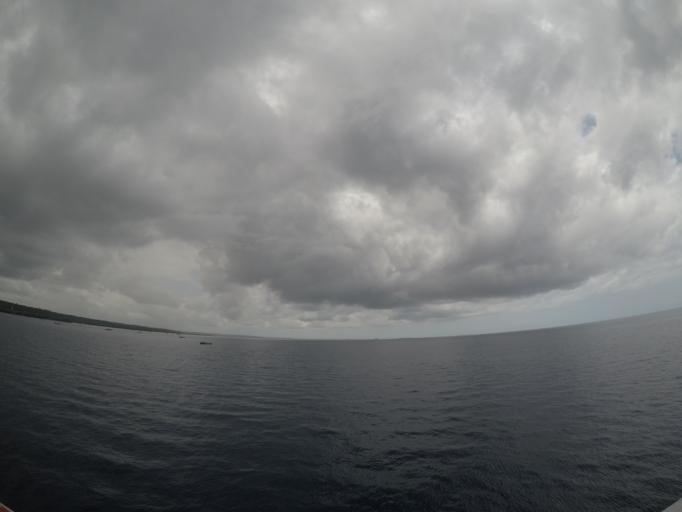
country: TZ
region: Zanzibar North
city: Mkokotoni
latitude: -5.9909
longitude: 39.1746
